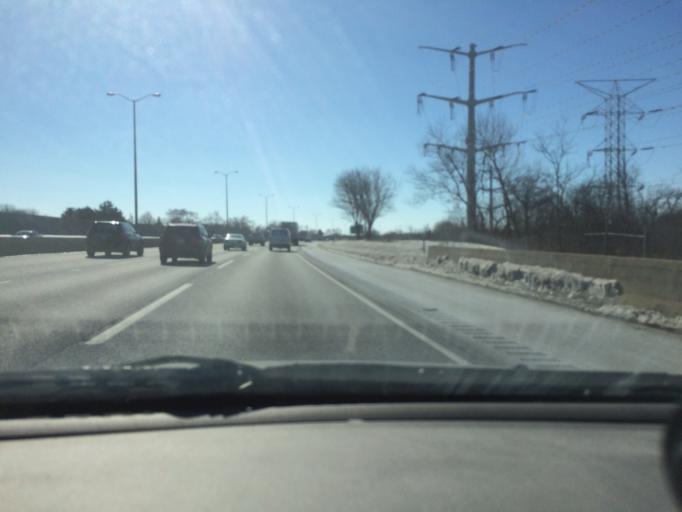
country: US
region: Illinois
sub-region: DuPage County
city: Lombard
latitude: 41.8768
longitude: -88.0333
